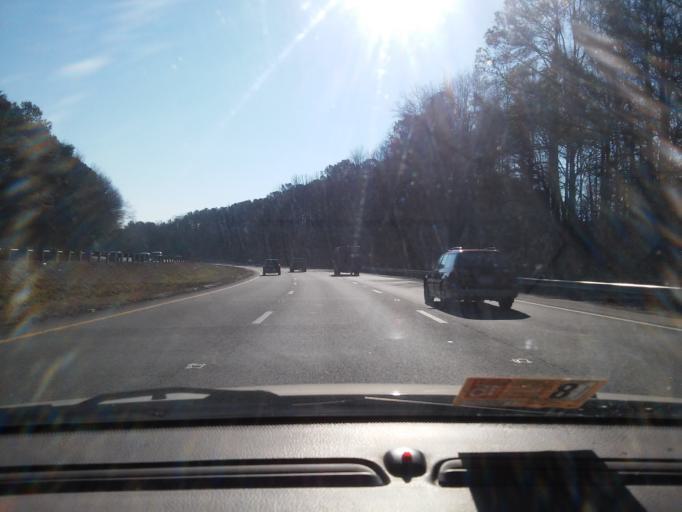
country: US
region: Virginia
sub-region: Henrico County
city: Dumbarton
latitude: 37.6006
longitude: -77.4997
